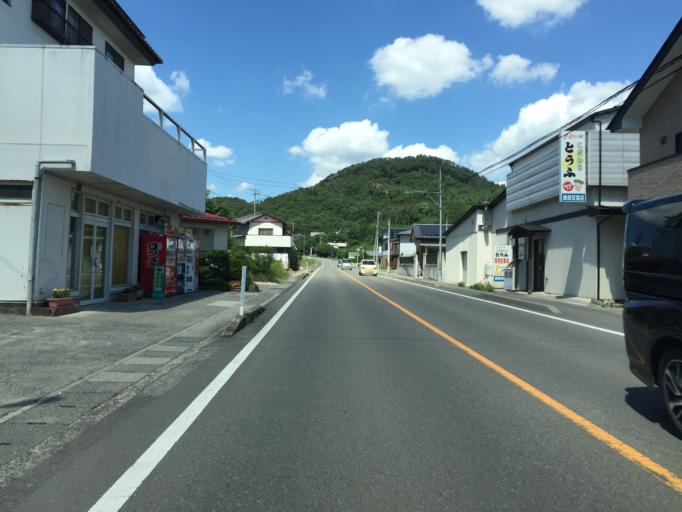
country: JP
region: Fukushima
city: Nihommatsu
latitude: 37.6341
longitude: 140.4639
